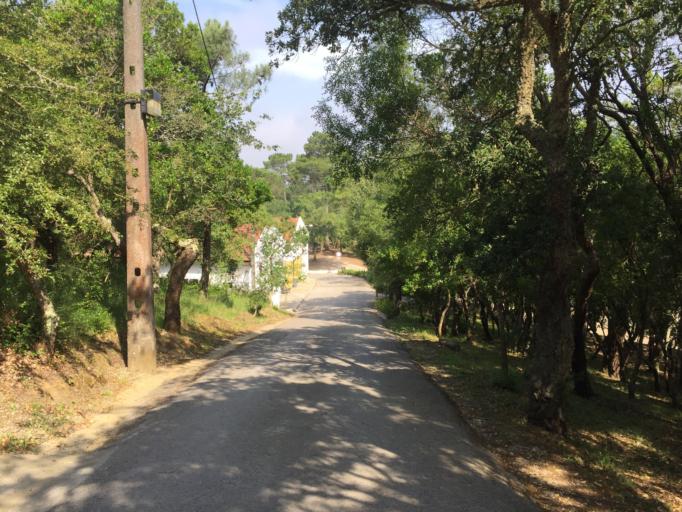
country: PT
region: Lisbon
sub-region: Mafra
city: Milharado
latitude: 38.9015
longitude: -9.1835
